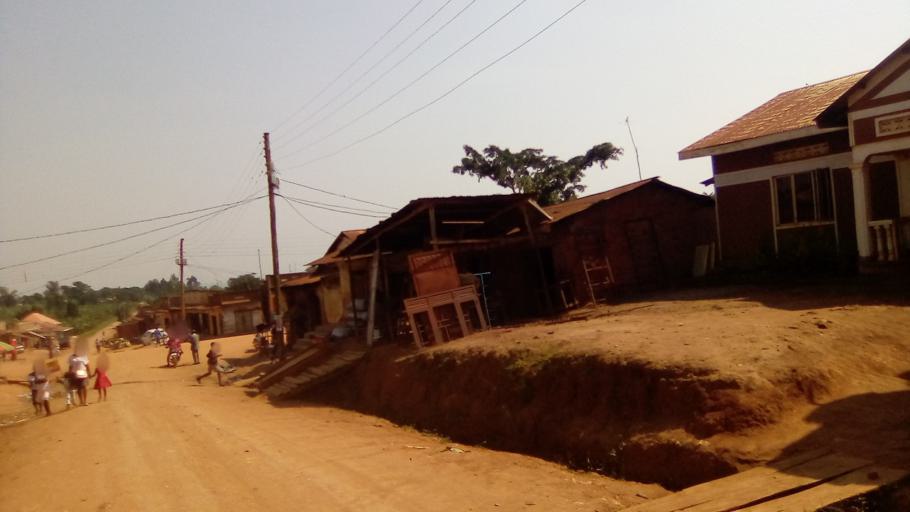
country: UG
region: Central Region
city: Masaka
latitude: -0.2691
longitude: 31.6469
